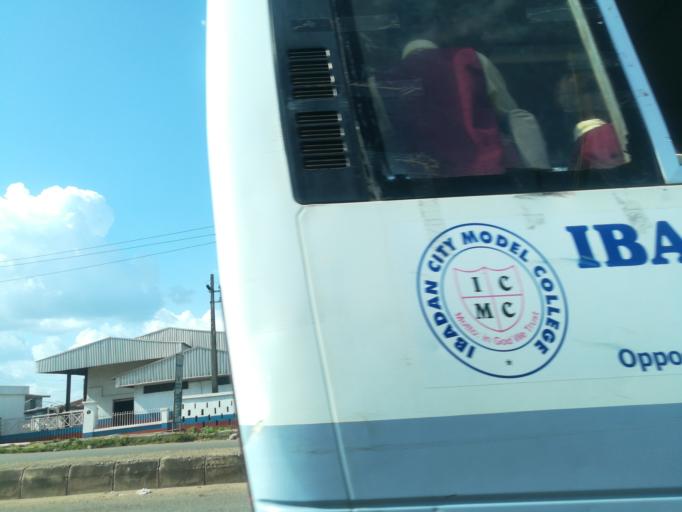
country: NG
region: Oyo
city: Egbeda
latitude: 7.4277
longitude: 3.9991
